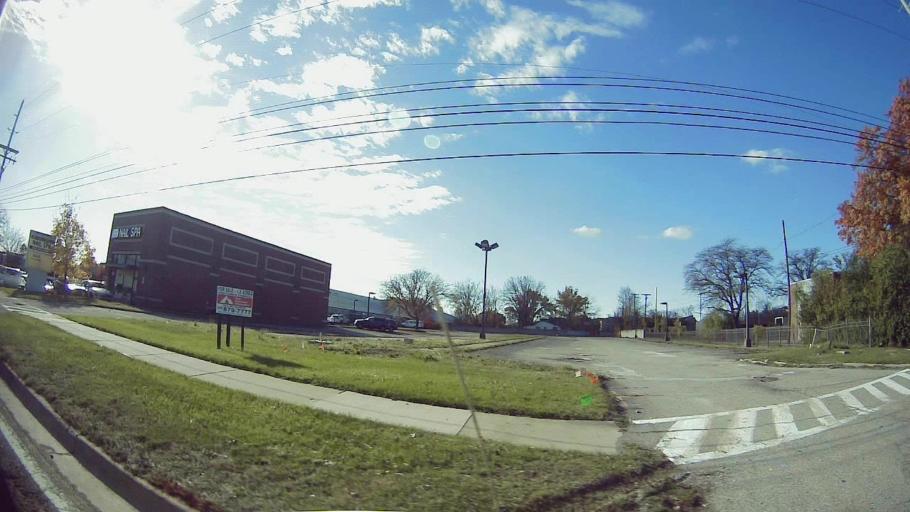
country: US
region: Michigan
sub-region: Oakland County
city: Beverly Hills
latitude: 42.5222
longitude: -83.2237
